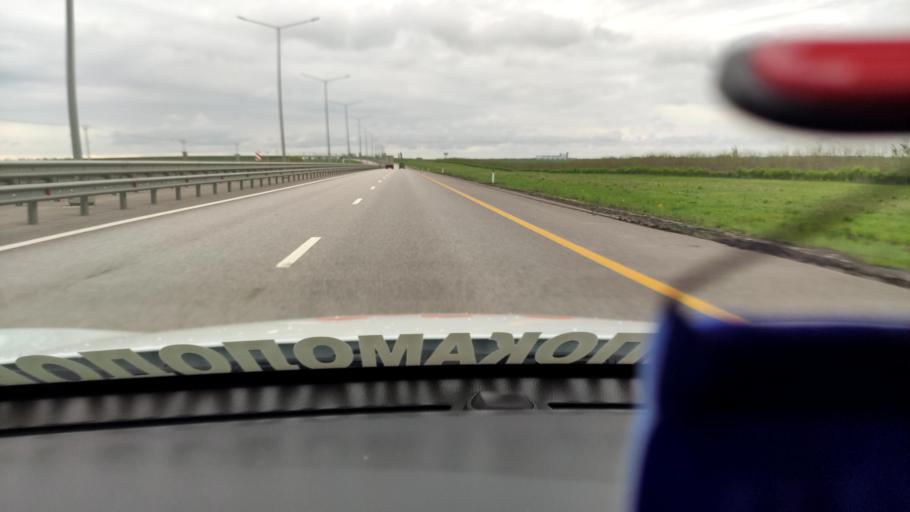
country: RU
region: Voronezj
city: Novaya Usman'
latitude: 51.5956
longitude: 39.3573
